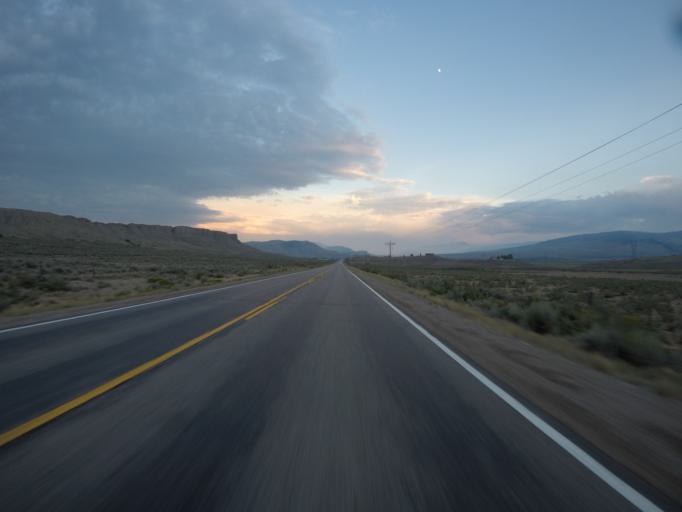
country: US
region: Colorado
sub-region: Grand County
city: Kremmling
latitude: 40.0731
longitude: -106.4090
